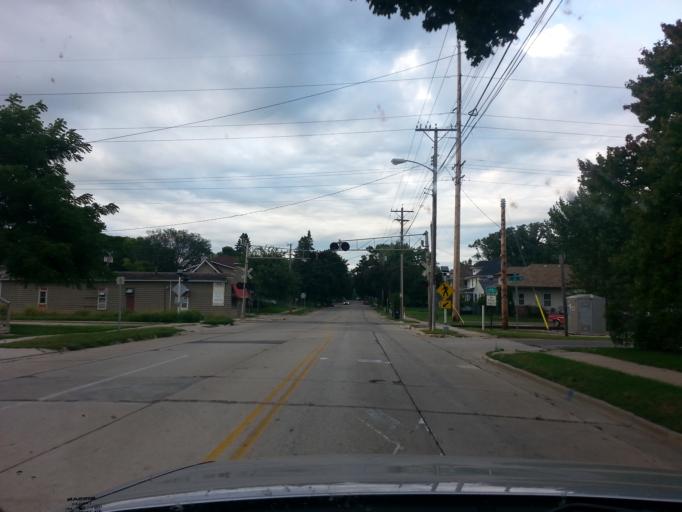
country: US
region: Minnesota
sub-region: Olmsted County
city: Rochester
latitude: 44.0243
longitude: -92.4488
